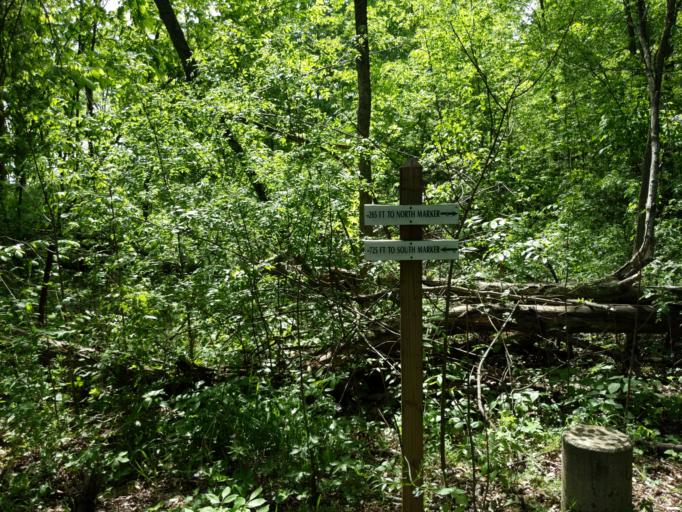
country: US
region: Michigan
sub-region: Ingham County
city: Leslie
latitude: 42.4241
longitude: -84.3647
